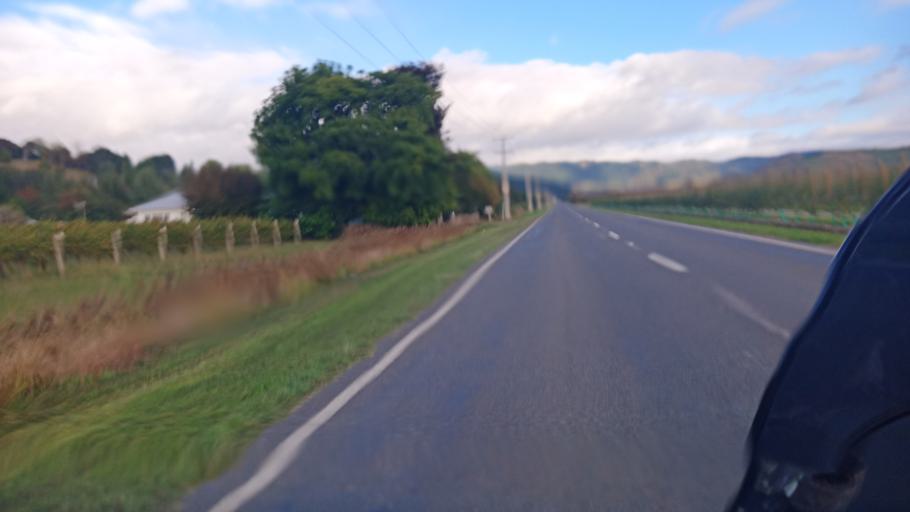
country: NZ
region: Gisborne
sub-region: Gisborne District
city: Gisborne
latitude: -38.6321
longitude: 177.8794
